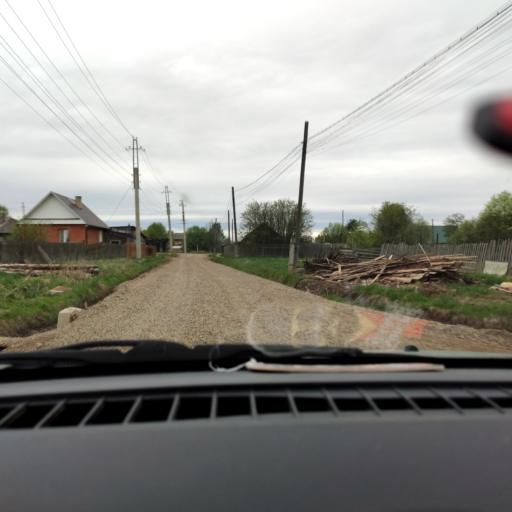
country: RU
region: Perm
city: Kudymkar
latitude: 59.0136
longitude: 54.6247
